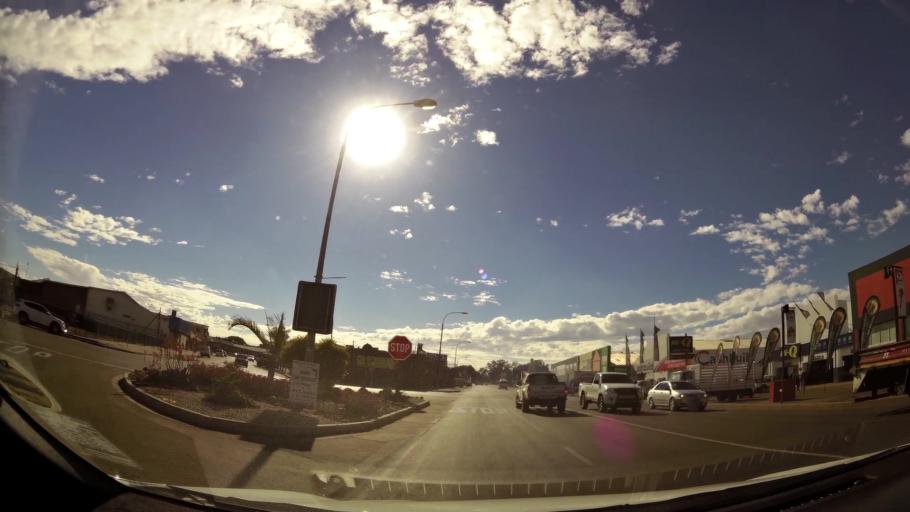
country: ZA
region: Limpopo
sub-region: Waterberg District Municipality
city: Bela-Bela
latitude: -24.8861
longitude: 28.2968
